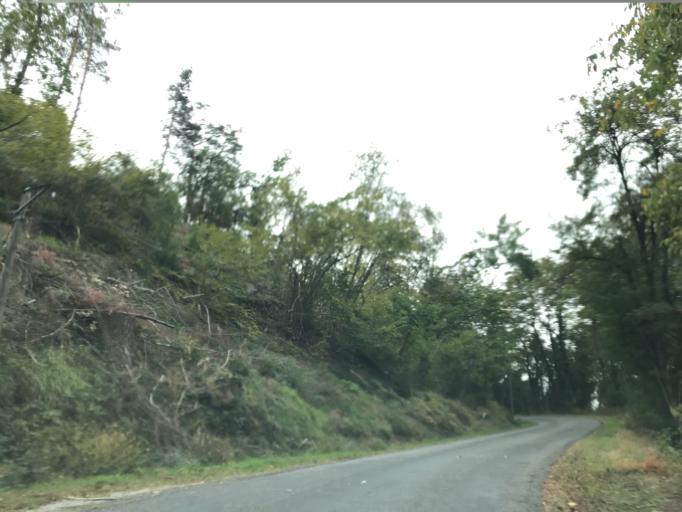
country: FR
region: Auvergne
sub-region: Departement du Puy-de-Dome
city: Thiers
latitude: 45.8440
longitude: 3.5536
